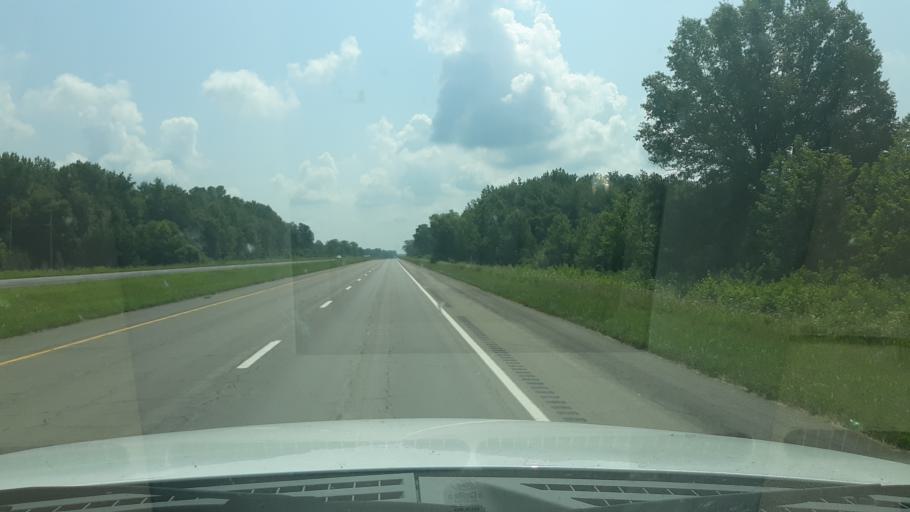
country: US
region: Illinois
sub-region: Saline County
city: Carrier Mills
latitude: 37.7333
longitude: -88.6627
